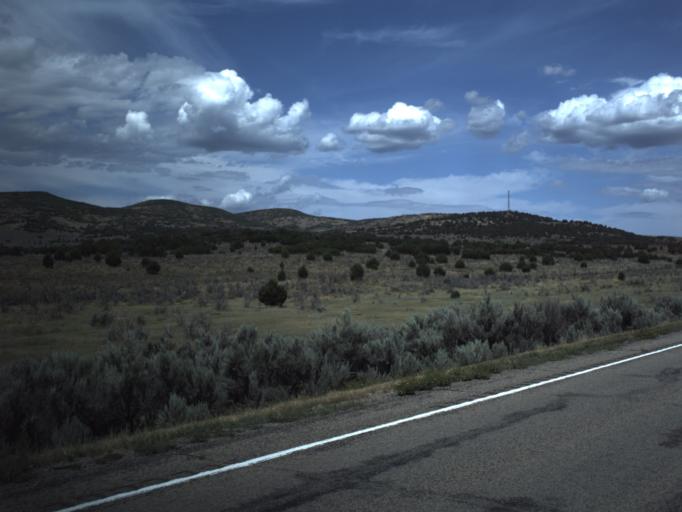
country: US
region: Utah
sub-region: Sanpete County
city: Fairview
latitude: 39.6740
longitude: -111.4562
